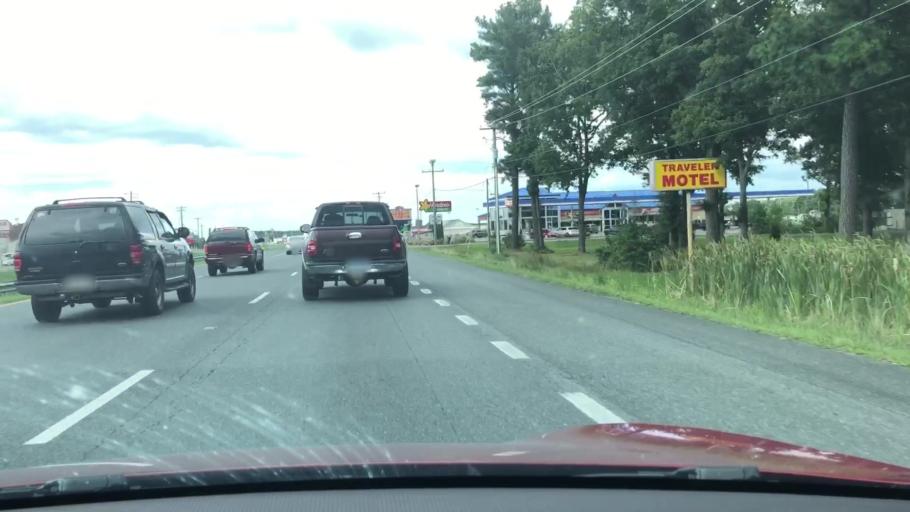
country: US
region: Delaware
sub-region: Sussex County
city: Delmar
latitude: 38.4518
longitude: -75.5587
